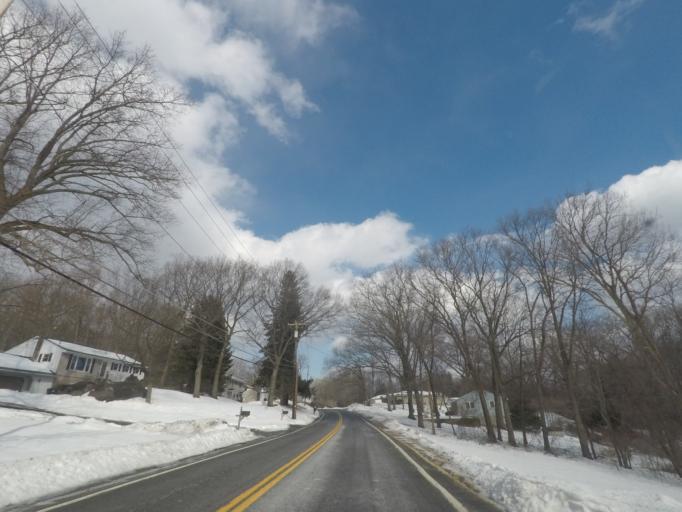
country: US
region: New York
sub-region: Albany County
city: Cohoes
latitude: 42.8114
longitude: -73.7505
